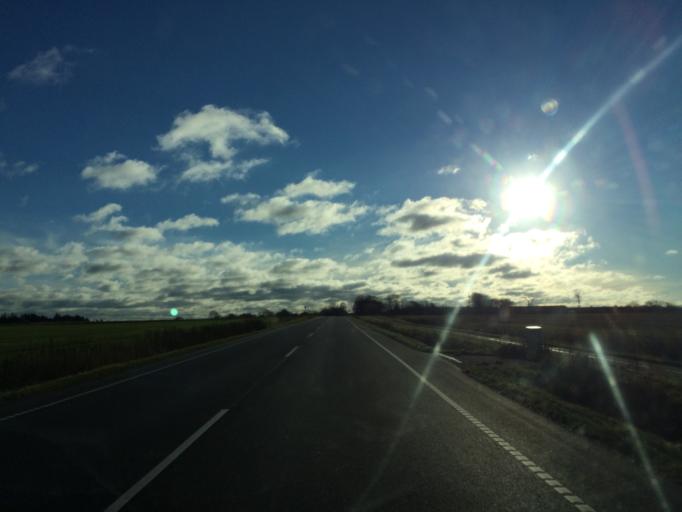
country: DK
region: Central Jutland
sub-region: Herning Kommune
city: Kibaek
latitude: 56.0193
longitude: 8.8514
